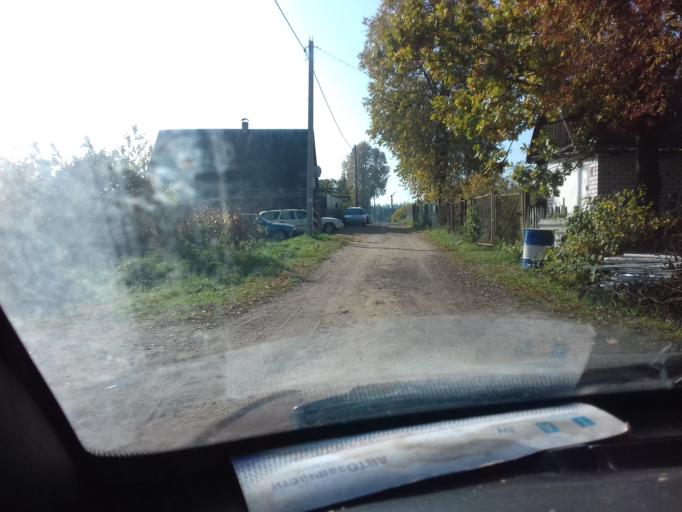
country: BY
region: Minsk
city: Hatava
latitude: 53.7676
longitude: 27.6507
